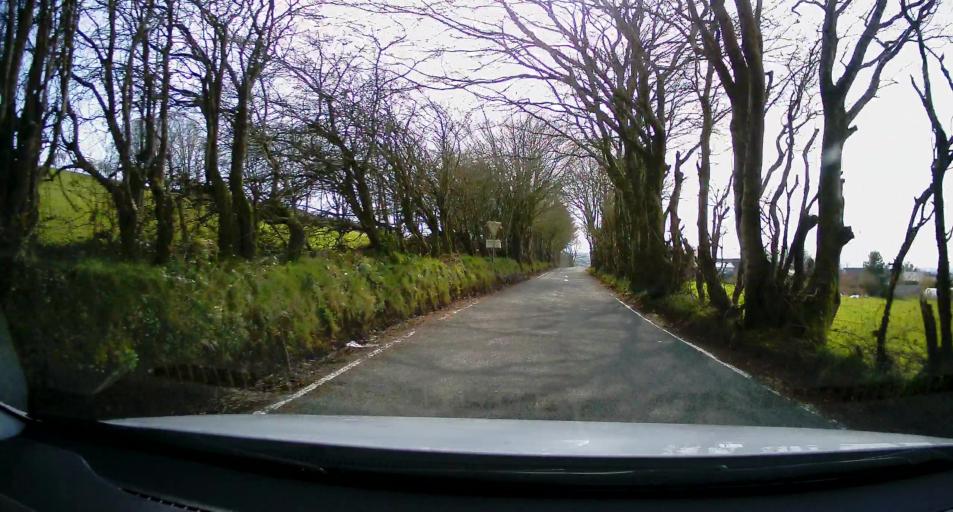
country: GB
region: Wales
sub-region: County of Ceredigion
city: Llanon
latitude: 52.2522
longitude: -4.0881
